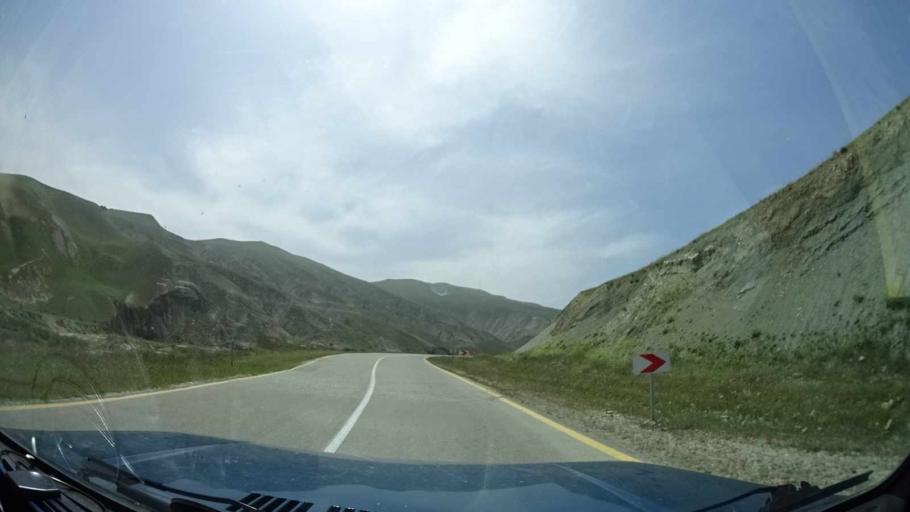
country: AZ
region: Xizi
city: Kilyazi
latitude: 40.8514
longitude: 49.3094
